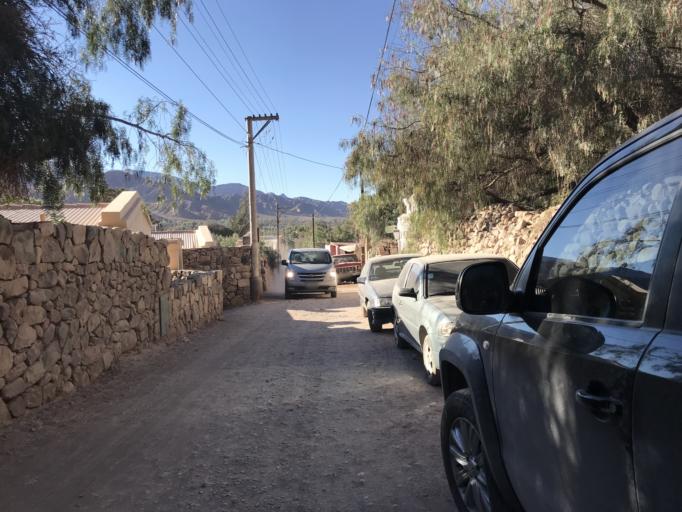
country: AR
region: Jujuy
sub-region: Departamento de Tilcara
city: Tilcara
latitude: -23.5795
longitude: -65.3961
